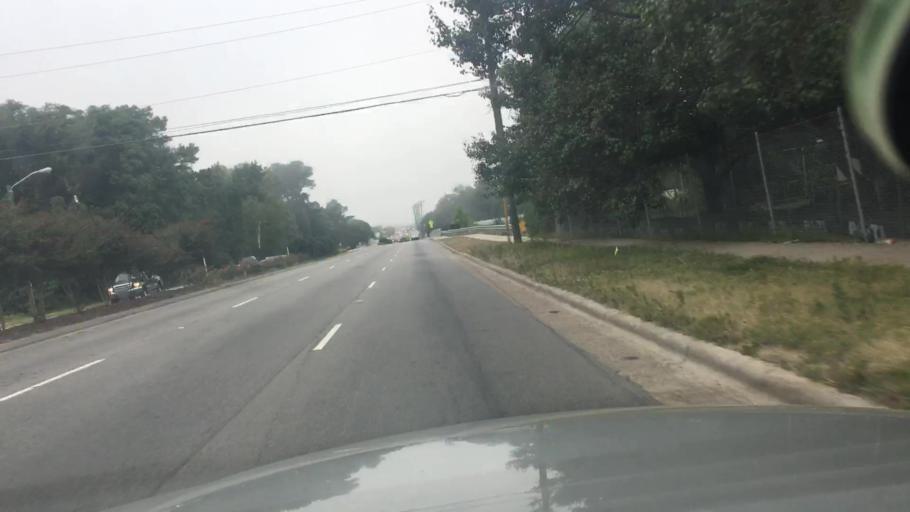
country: US
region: North Carolina
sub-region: Cumberland County
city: Fayetteville
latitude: 35.0547
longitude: -78.8697
